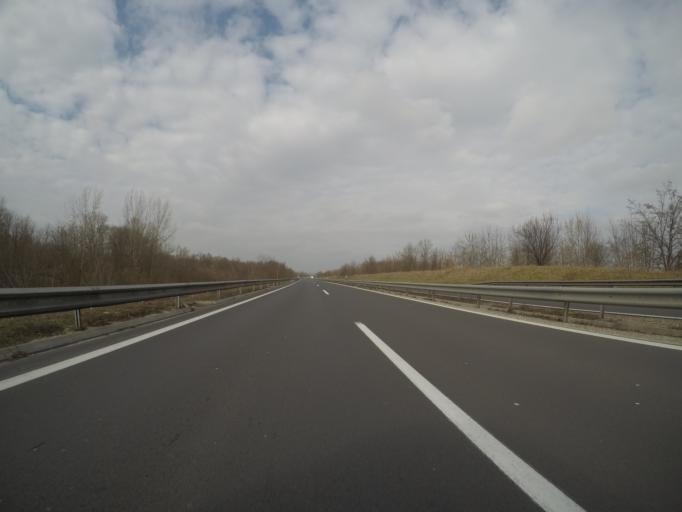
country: SI
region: Murska Sobota
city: Bakovci
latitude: 46.6106
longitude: 16.1300
